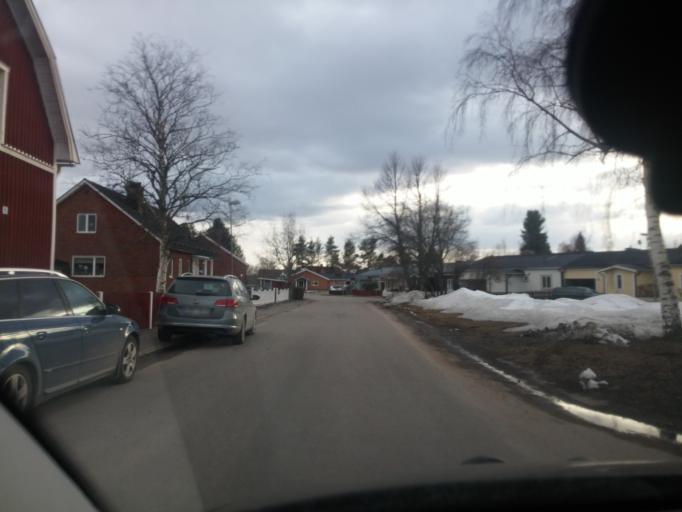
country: SE
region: Gaevleborg
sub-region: Ljusdals Kommun
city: Ljusdal
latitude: 61.8334
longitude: 16.0978
